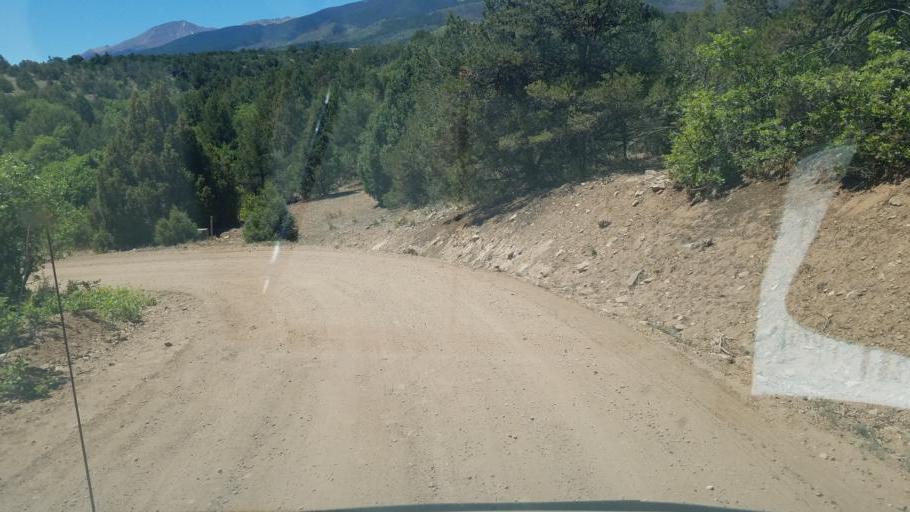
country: US
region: Colorado
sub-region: Custer County
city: Westcliffe
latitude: 38.3047
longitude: -105.6732
